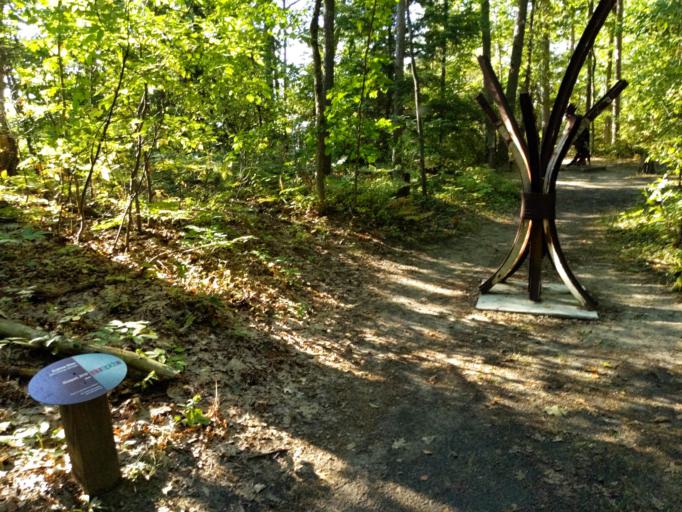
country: US
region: Michigan
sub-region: Antrim County
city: Elk Rapids
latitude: 44.8880
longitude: -85.4232
